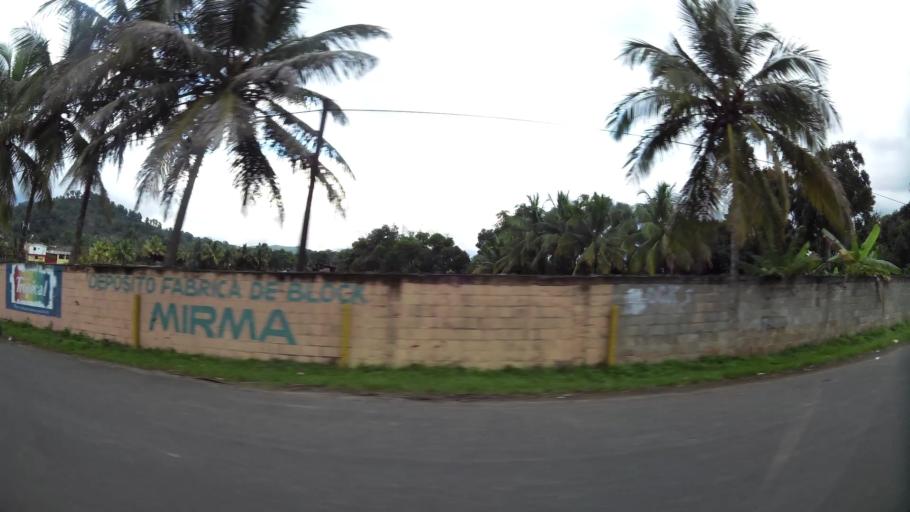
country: DO
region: San Cristobal
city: Villa Altagracia
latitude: 18.6512
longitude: -70.1693
